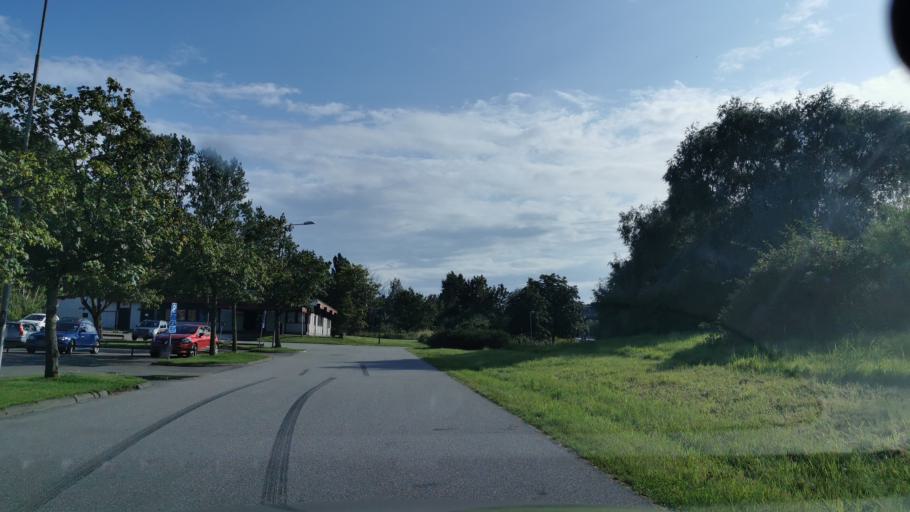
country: SE
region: Vaestra Goetaland
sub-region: Goteborg
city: Majorna
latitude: 57.6406
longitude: 11.9329
